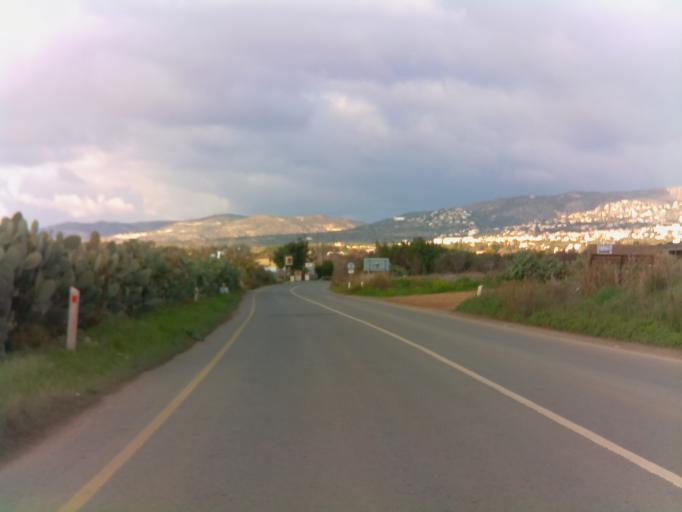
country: CY
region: Pafos
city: Kissonerga
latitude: 34.8137
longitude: 32.4108
